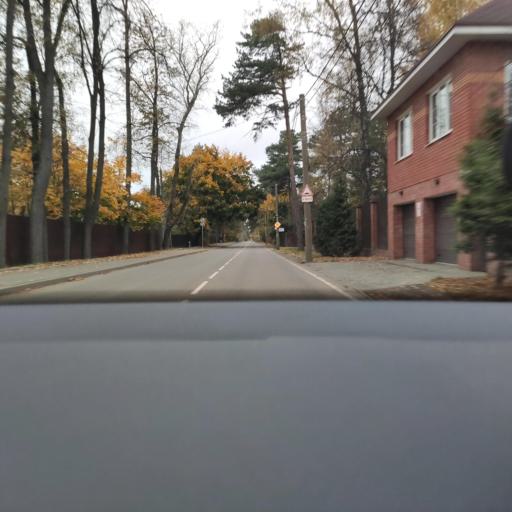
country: RU
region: Moscow
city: Mikhalkovo
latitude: 55.6684
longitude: 37.4188
